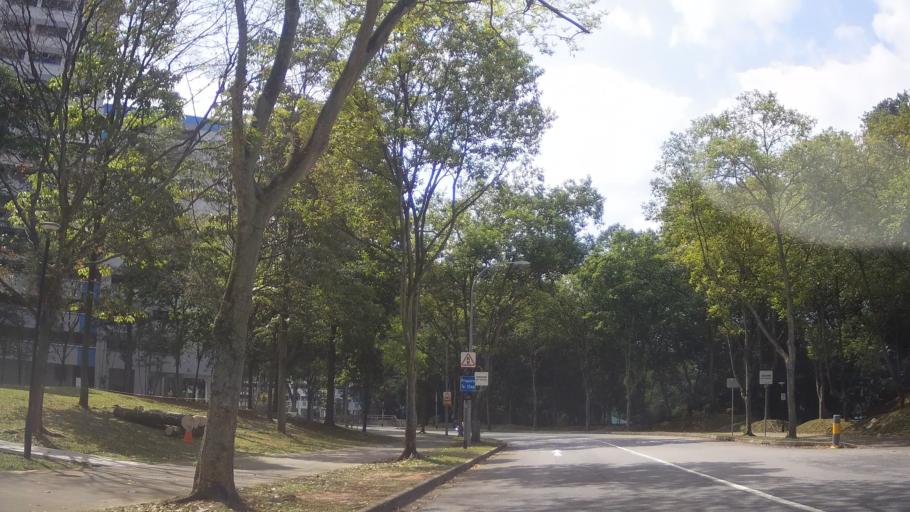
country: MY
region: Johor
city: Johor Bahru
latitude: 1.3832
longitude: 103.7662
